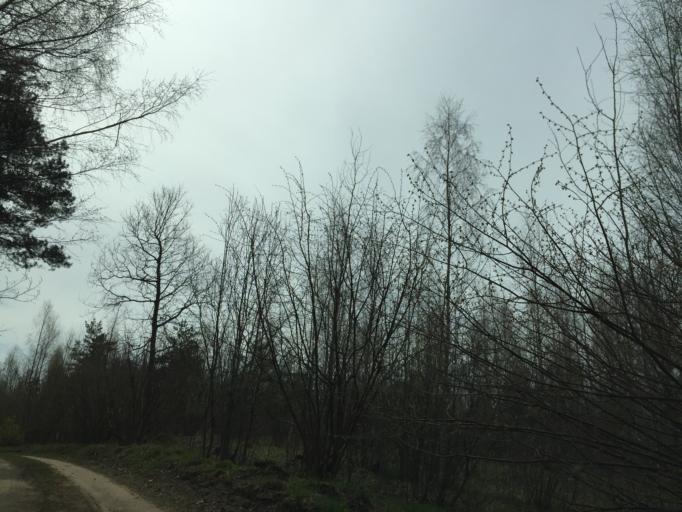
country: LV
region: Ludzas Rajons
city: Ludza
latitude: 56.5300
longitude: 27.5820
